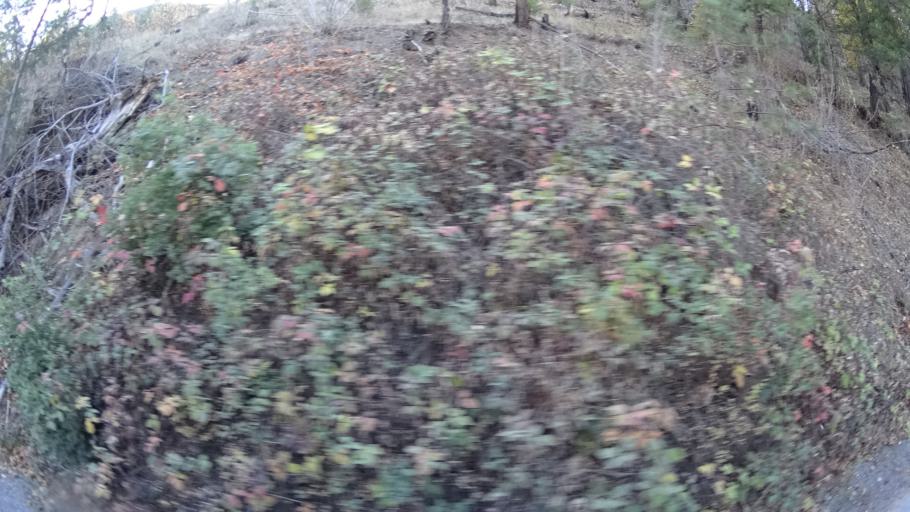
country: US
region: California
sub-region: Siskiyou County
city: Yreka
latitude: 41.8473
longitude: -122.6926
